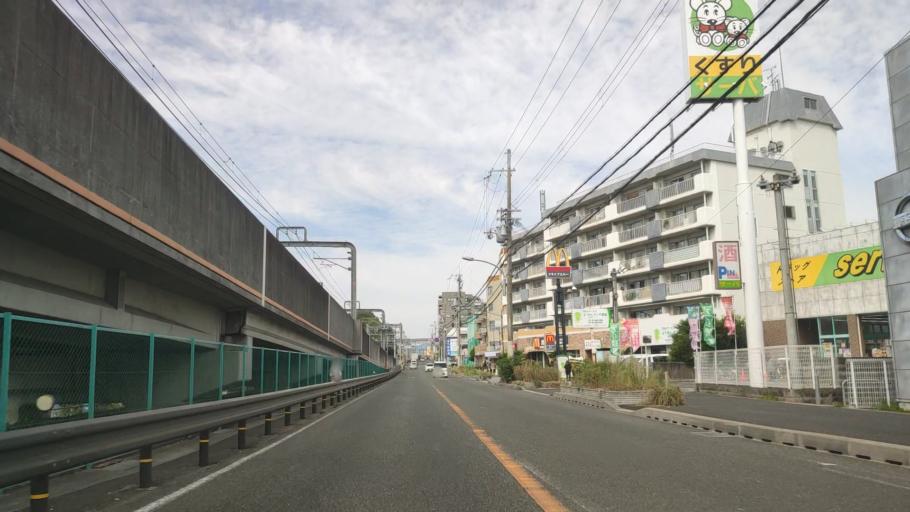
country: JP
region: Osaka
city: Toyonaka
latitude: 34.7904
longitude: 135.4549
